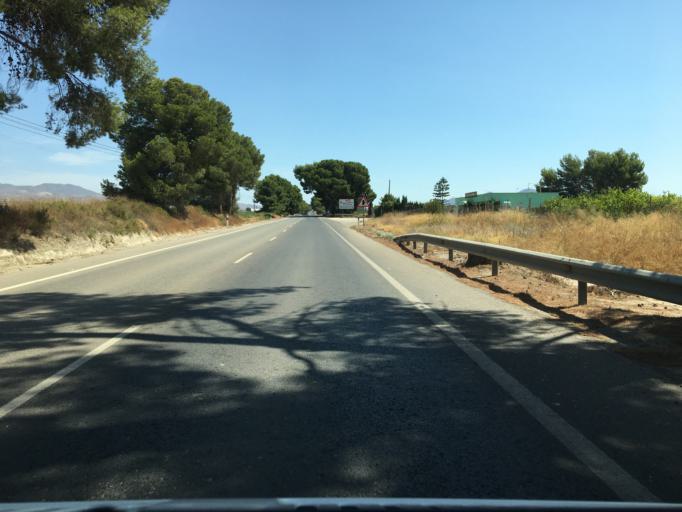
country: ES
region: Andalusia
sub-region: Provincia de Almeria
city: Huercal-Overa
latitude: 37.4198
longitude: -1.9217
